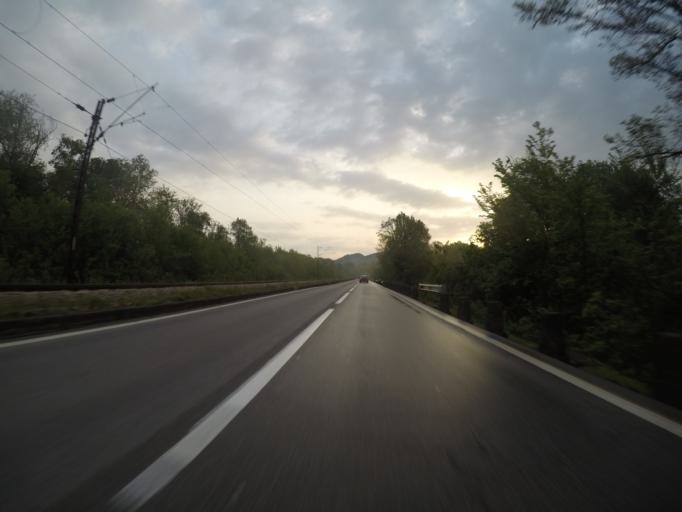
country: ME
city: Mojanovici
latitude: 42.3031
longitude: 19.1696
